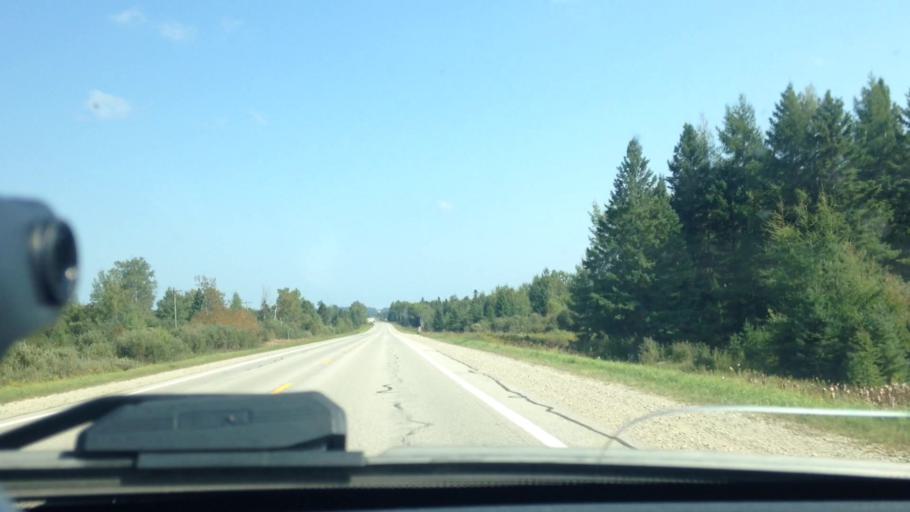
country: US
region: Michigan
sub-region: Luce County
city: Newberry
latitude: 46.3102
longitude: -85.6245
